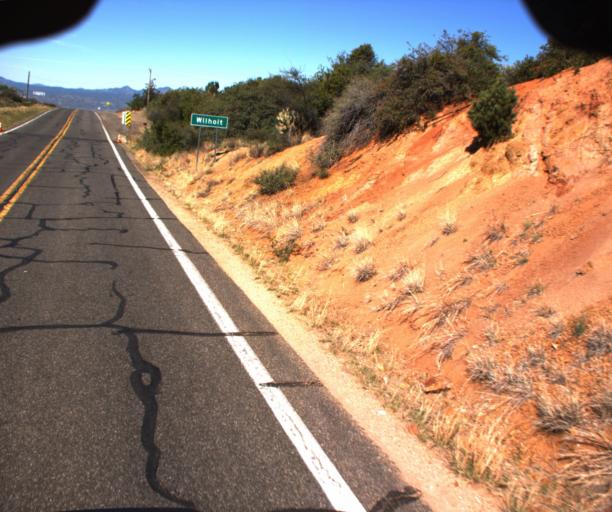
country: US
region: Arizona
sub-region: Yavapai County
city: Prescott
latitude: 34.4269
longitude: -112.5849
